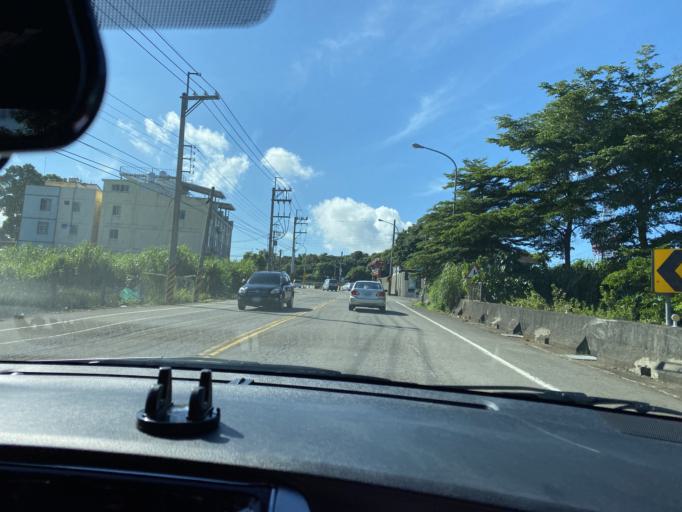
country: TW
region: Taiwan
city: Zhongxing New Village
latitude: 23.9683
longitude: 120.6245
